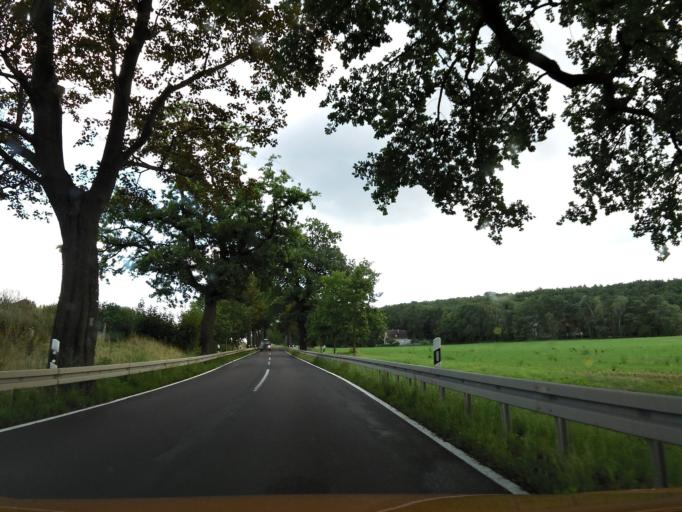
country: DE
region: Brandenburg
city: Potsdam
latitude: 52.4563
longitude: 13.0395
